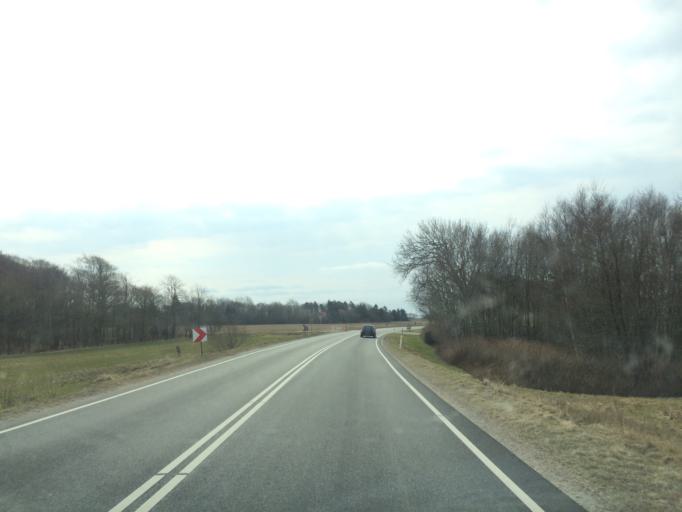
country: DK
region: Central Jutland
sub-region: Ringkobing-Skjern Kommune
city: Skjern
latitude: 55.9933
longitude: 8.5075
